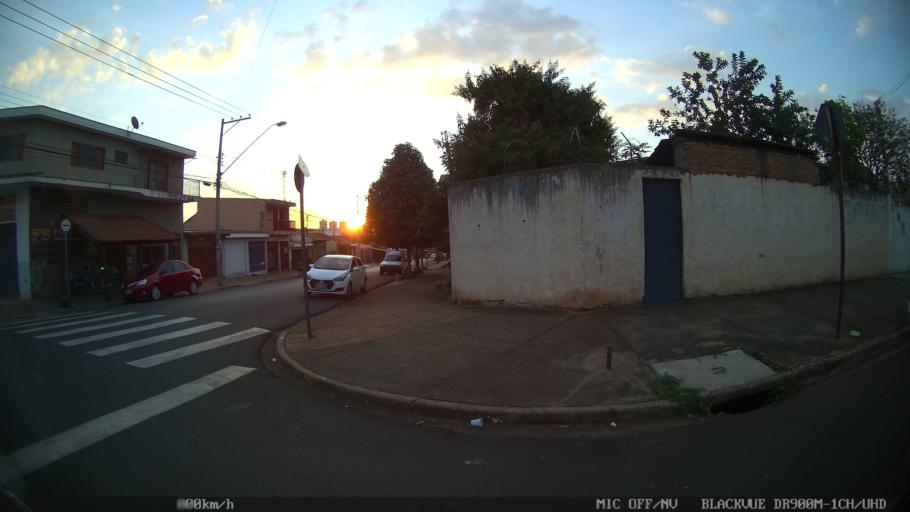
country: BR
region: Sao Paulo
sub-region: Ribeirao Preto
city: Ribeirao Preto
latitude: -21.1417
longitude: -47.8240
